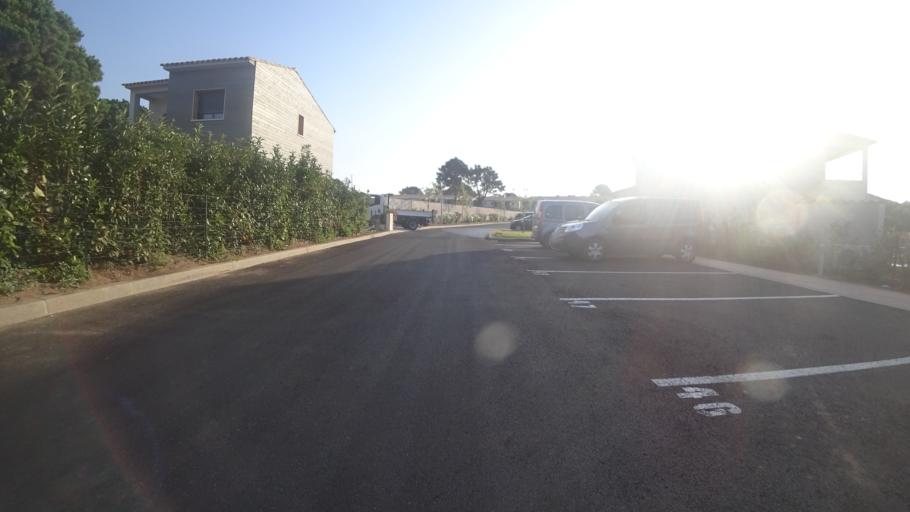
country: FR
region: Corsica
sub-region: Departement de la Corse-du-Sud
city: Porto-Vecchio
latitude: 41.6283
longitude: 9.3348
